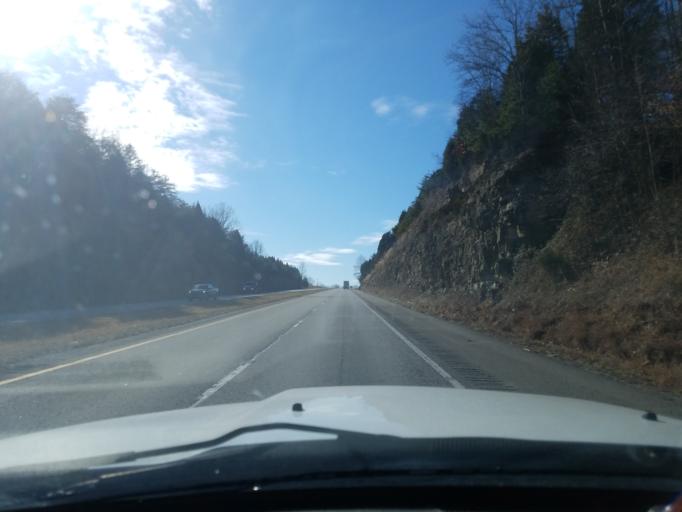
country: US
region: Kentucky
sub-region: Grayson County
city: Leitchfield
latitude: 37.5050
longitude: -86.1599
